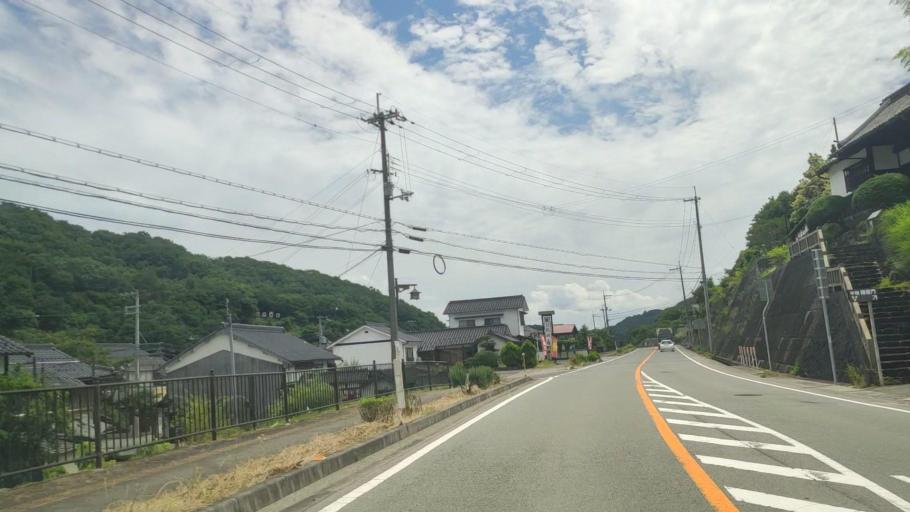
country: JP
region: Hyogo
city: Yamazakicho-nakabirose
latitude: 35.0441
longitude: 134.3699
